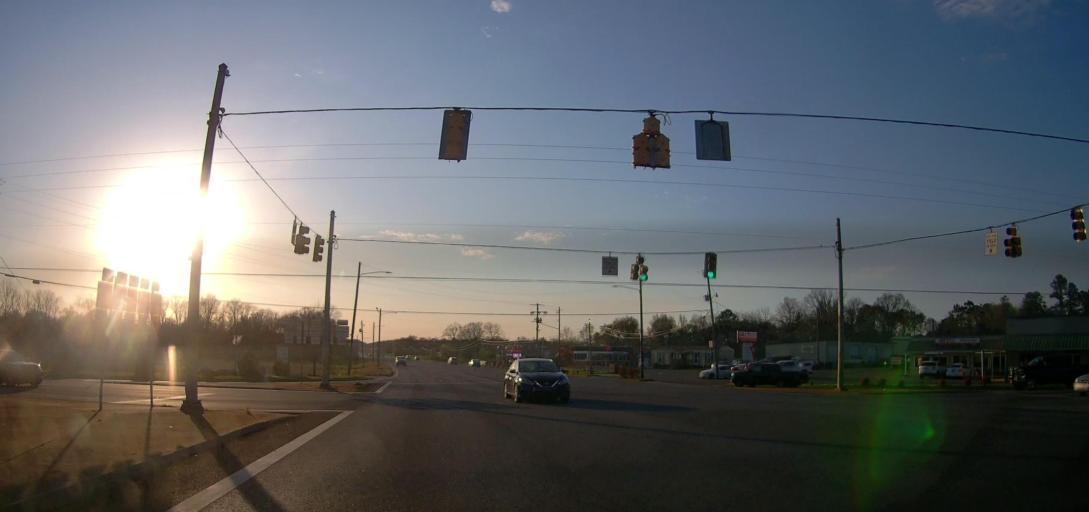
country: US
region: Alabama
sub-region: Shelby County
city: Harpersville
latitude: 33.3438
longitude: -86.4381
